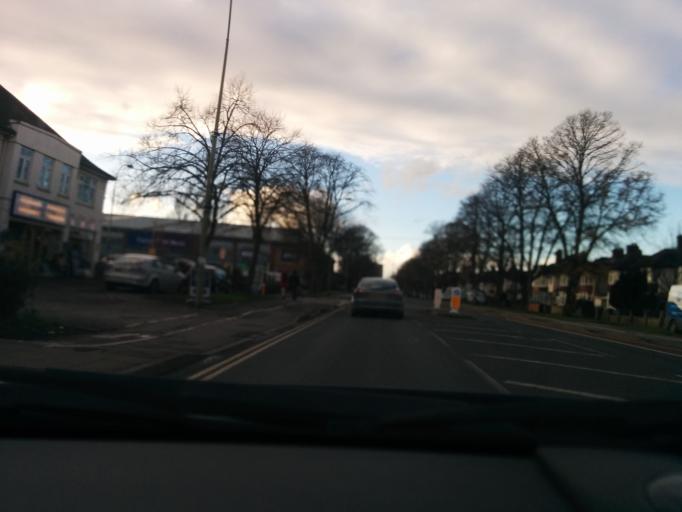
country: GB
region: England
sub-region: Oxfordshire
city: Oxford
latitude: 51.7528
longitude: -1.2843
